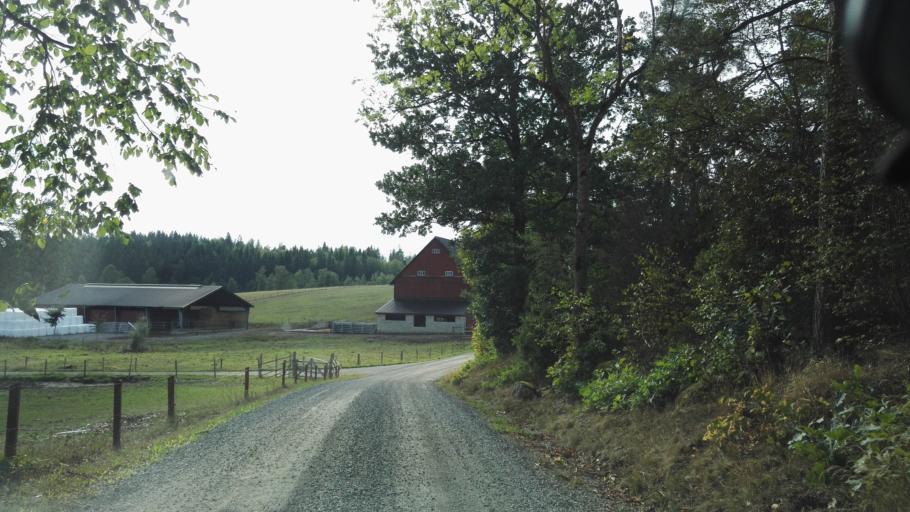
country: SE
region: Joenkoeping
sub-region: Vetlanda Kommun
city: Landsbro
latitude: 57.2361
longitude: 14.8412
